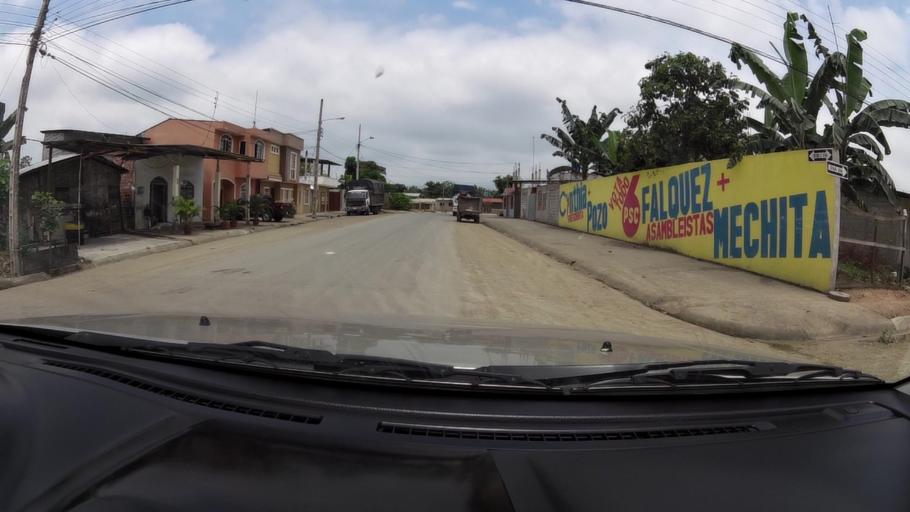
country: EC
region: El Oro
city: Pasaje
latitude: -3.2368
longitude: -79.8255
